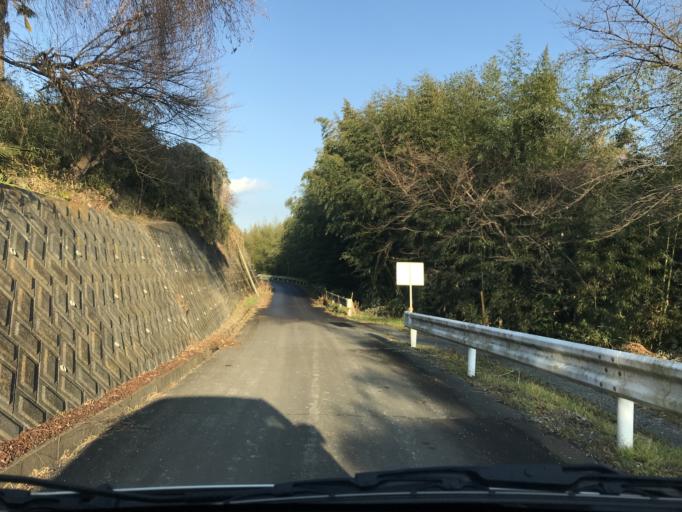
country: JP
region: Miyagi
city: Wakuya
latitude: 38.7028
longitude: 141.1353
